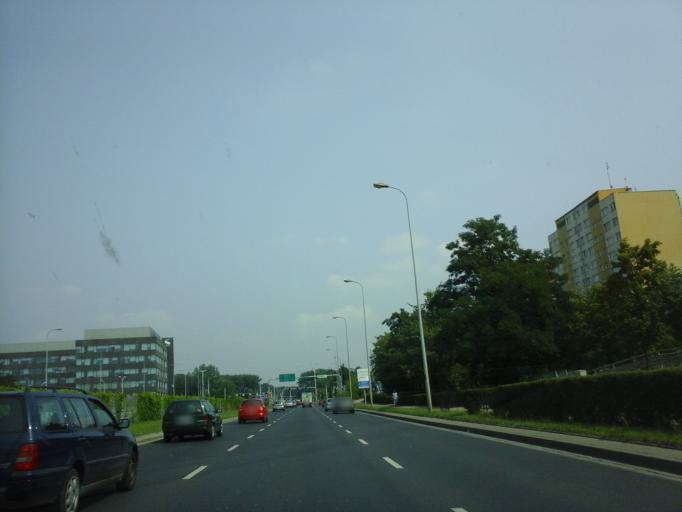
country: PL
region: Lower Silesian Voivodeship
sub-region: Powiat wroclawski
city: Wroclaw
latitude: 51.1245
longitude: 16.9775
